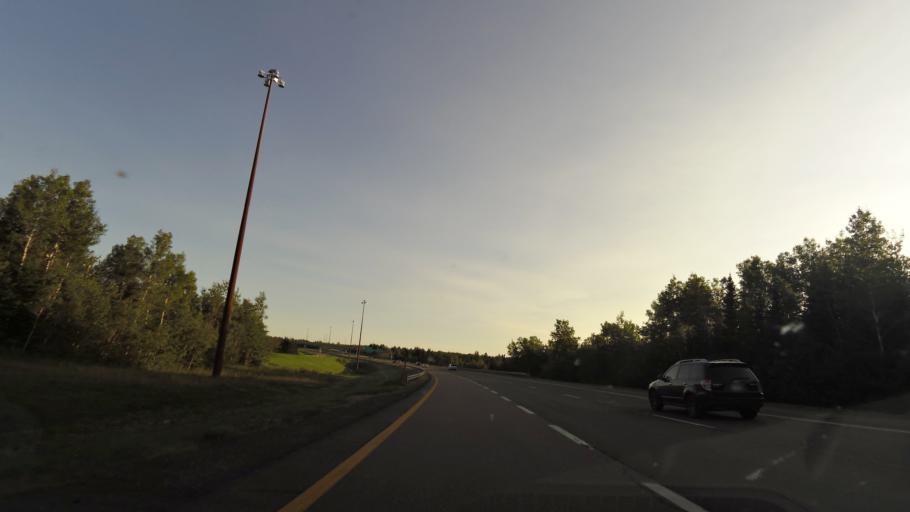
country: CA
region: New Brunswick
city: Salisbury
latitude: 45.9974
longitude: -65.1376
